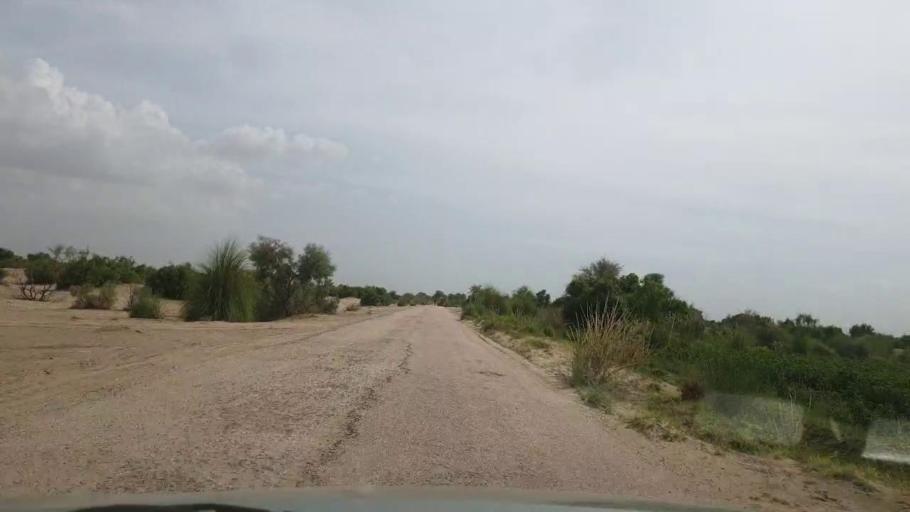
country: PK
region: Sindh
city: Kot Diji
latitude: 27.1235
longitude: 69.0269
